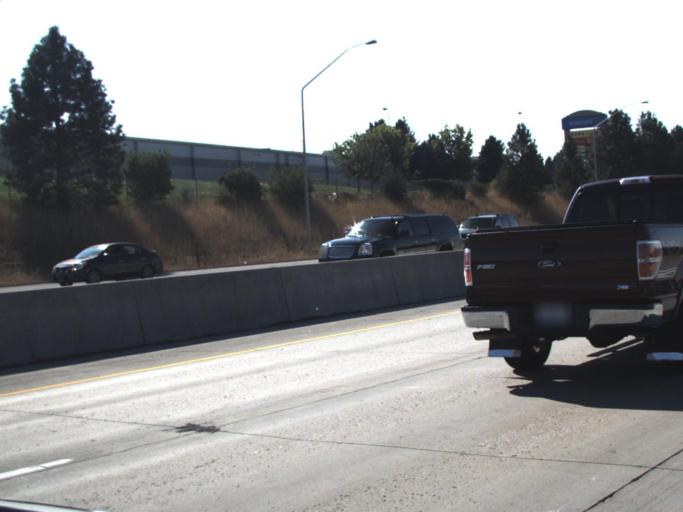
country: US
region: Washington
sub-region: Spokane County
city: Veradale
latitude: 47.6678
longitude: -117.1892
